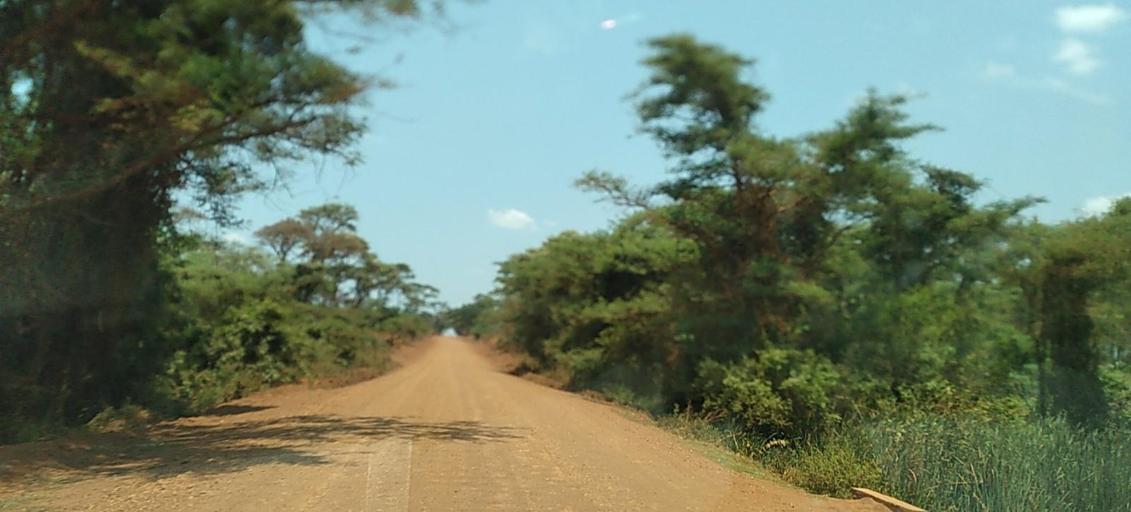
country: ZM
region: Copperbelt
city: Mpongwe
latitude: -13.5179
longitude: 27.9764
